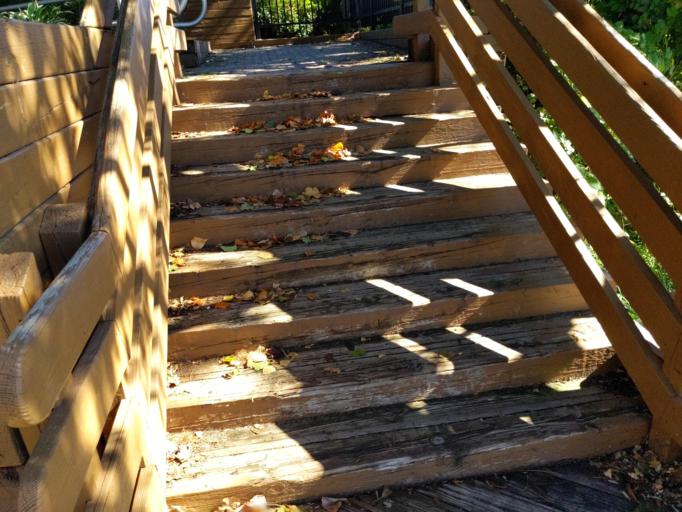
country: US
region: Michigan
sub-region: Antrim County
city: Elk Rapids
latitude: 44.8998
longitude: -85.4137
